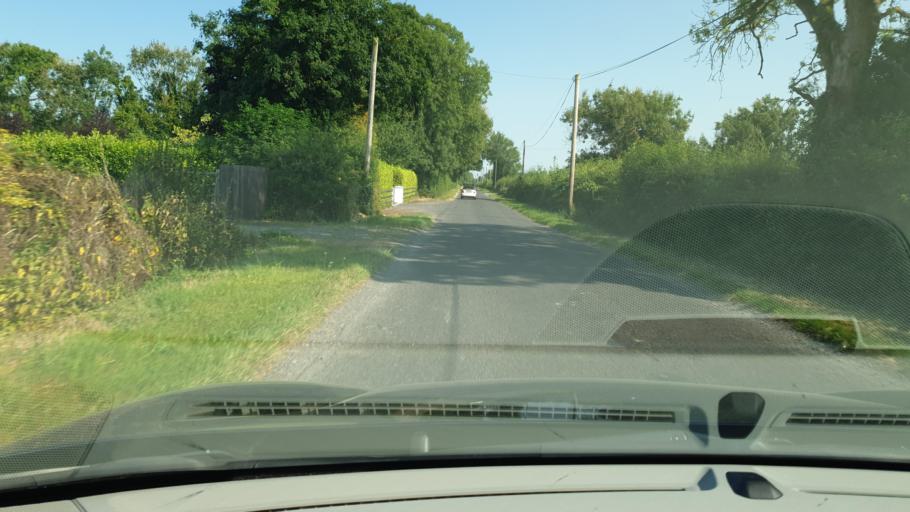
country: IE
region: Leinster
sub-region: An Mhi
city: Athboy
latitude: 53.6334
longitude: -6.9716
